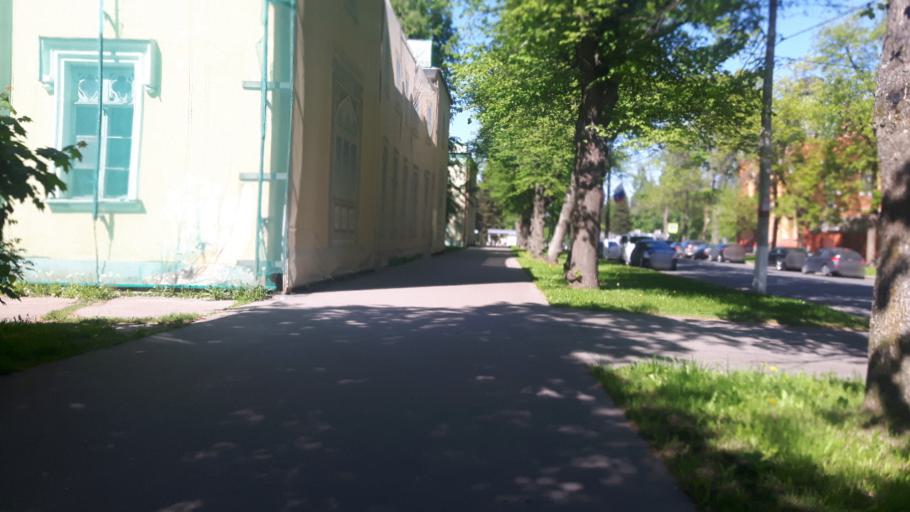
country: RU
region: St.-Petersburg
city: Peterhof
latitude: 59.8797
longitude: 29.9239
